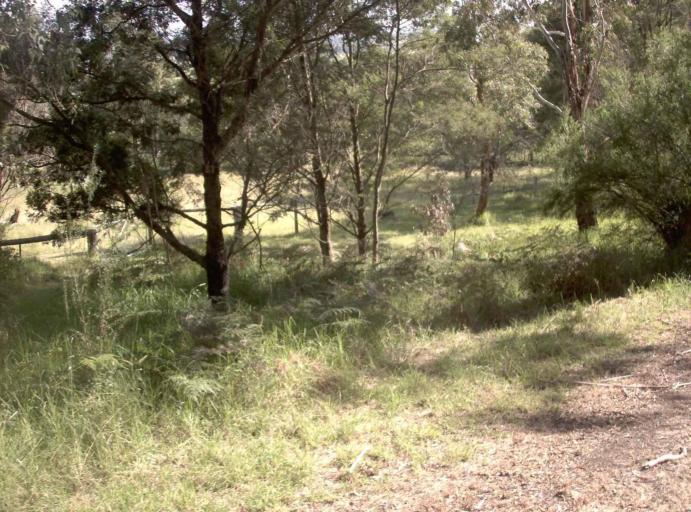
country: AU
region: Victoria
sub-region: East Gippsland
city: Lakes Entrance
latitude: -37.7433
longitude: 147.8154
